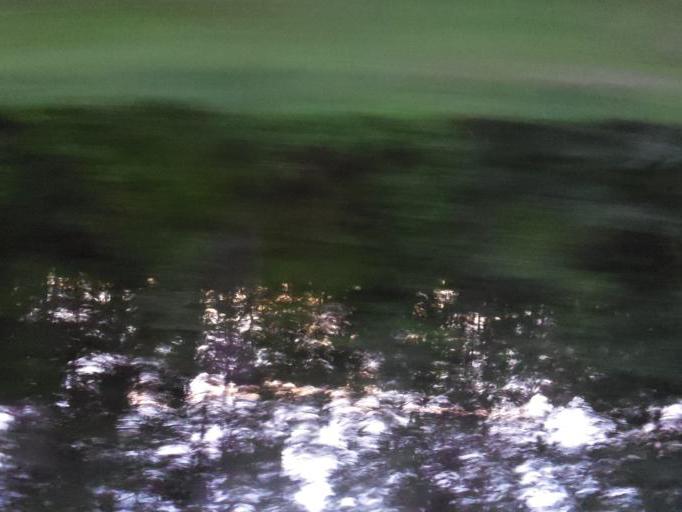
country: US
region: Georgia
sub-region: Camden County
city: Kingsland
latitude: 30.7599
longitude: -81.6874
